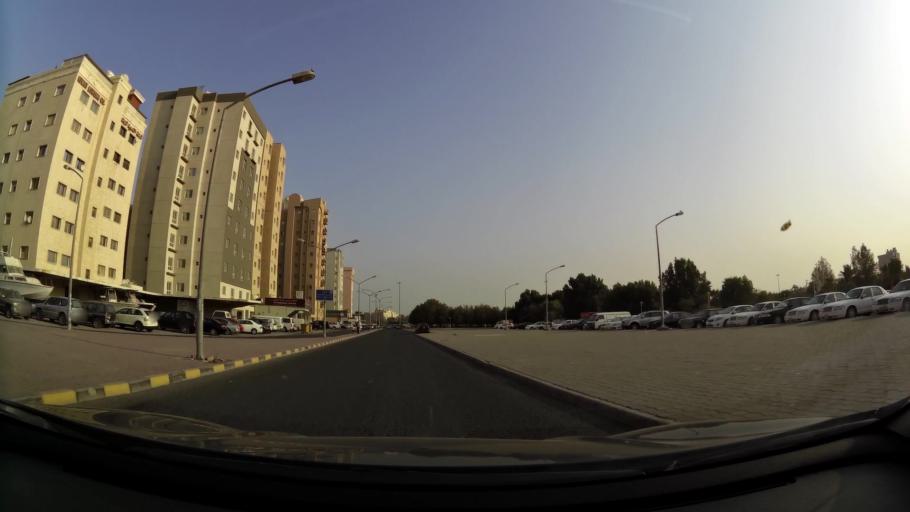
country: KW
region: Muhafazat Hawalli
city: As Salimiyah
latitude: 29.3269
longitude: 48.0674
